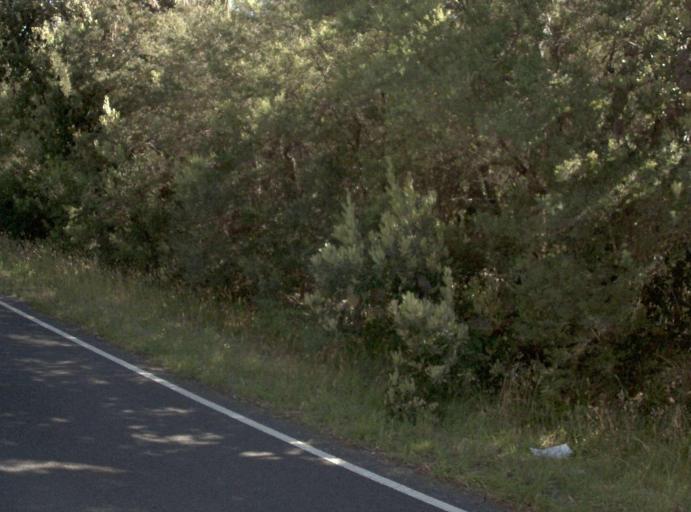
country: AU
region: Victoria
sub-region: Latrobe
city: Traralgon
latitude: -38.6567
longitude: 146.6797
